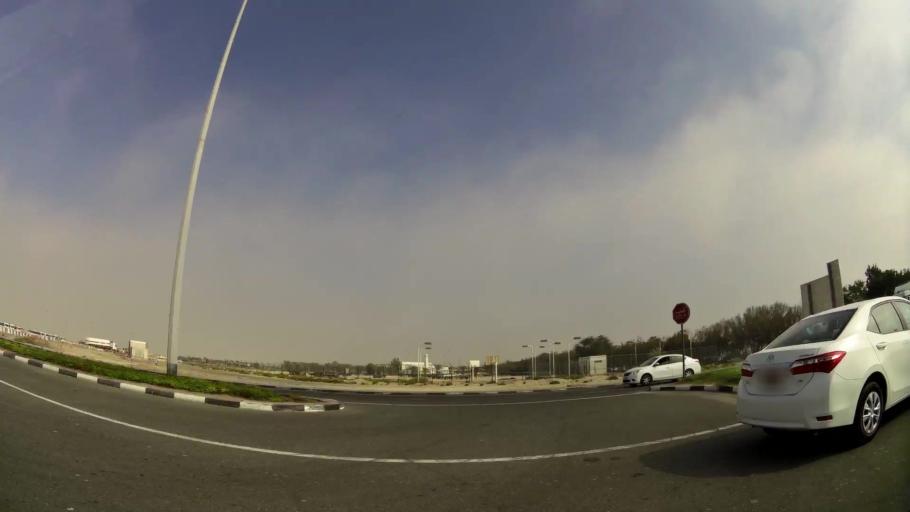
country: AE
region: Dubai
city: Dubai
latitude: 24.9590
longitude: 55.0519
